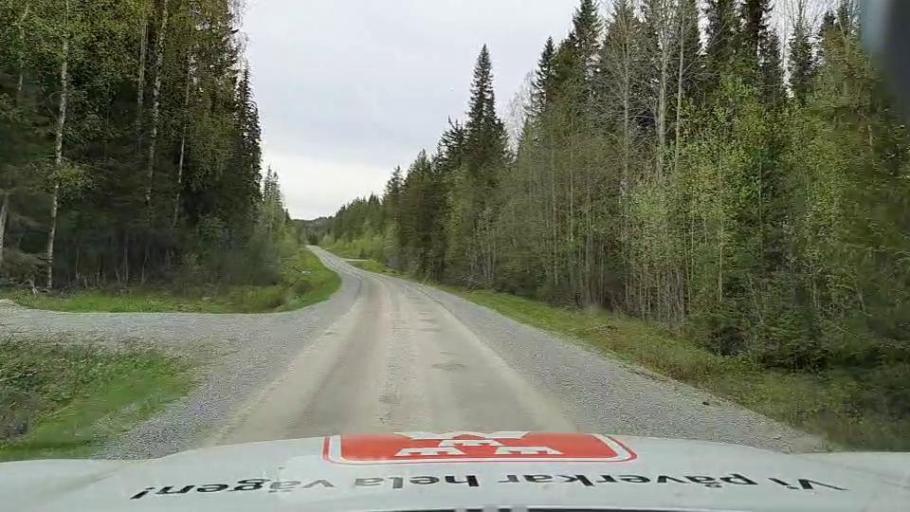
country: SE
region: Jaemtland
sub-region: OEstersunds Kommun
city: Brunflo
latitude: 62.6402
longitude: 14.9341
